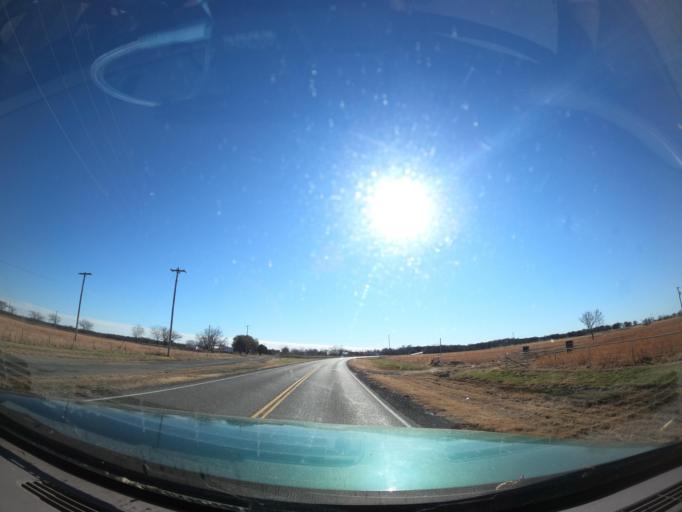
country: US
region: Oklahoma
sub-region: Muskogee County
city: Haskell
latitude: 35.6687
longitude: -95.6422
